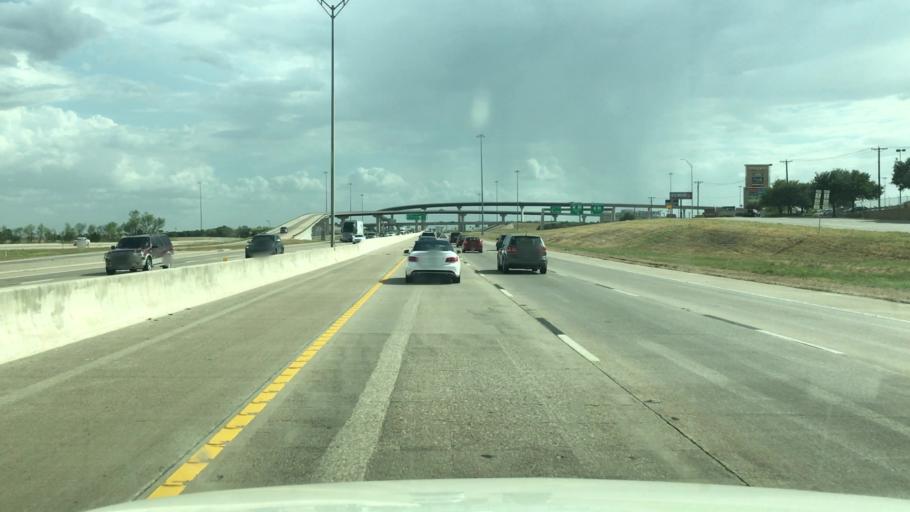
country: US
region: Texas
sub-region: McLennan County
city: Beverly Hills
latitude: 31.5000
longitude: -97.1471
